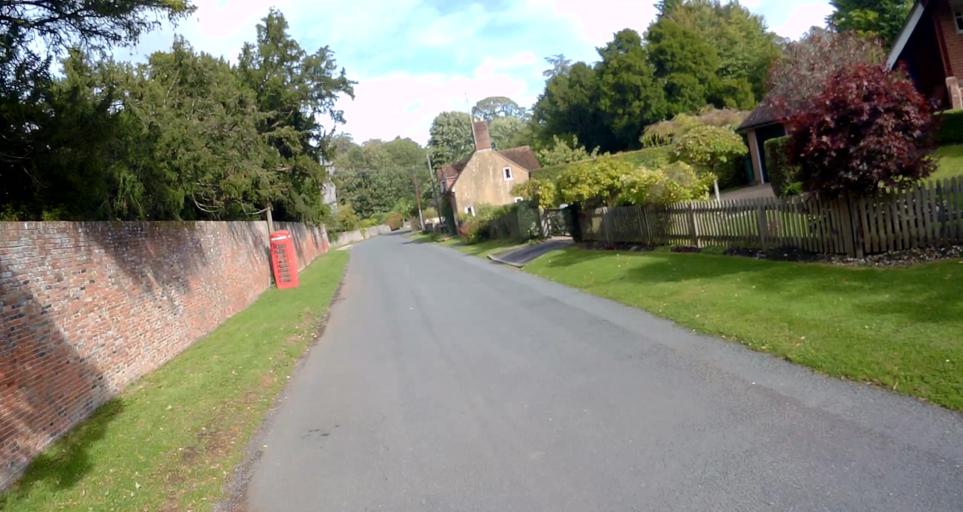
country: GB
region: England
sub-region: Hampshire
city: Kings Worthy
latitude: 51.0865
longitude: -1.2414
